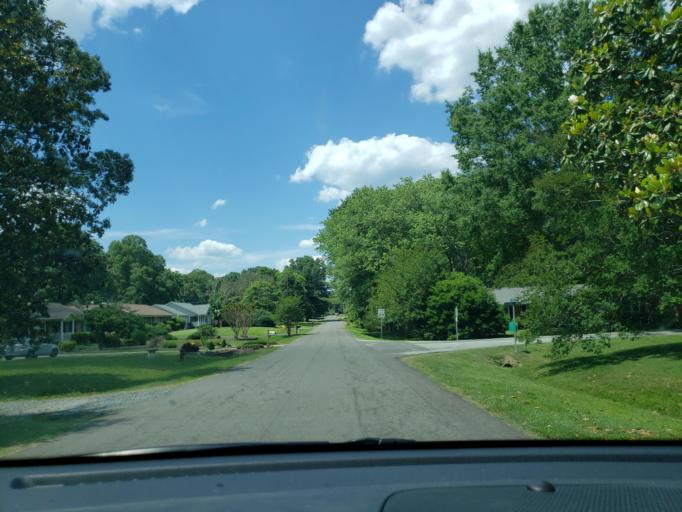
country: US
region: North Carolina
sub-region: Orange County
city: Chapel Hill
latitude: 35.9717
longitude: -78.9876
